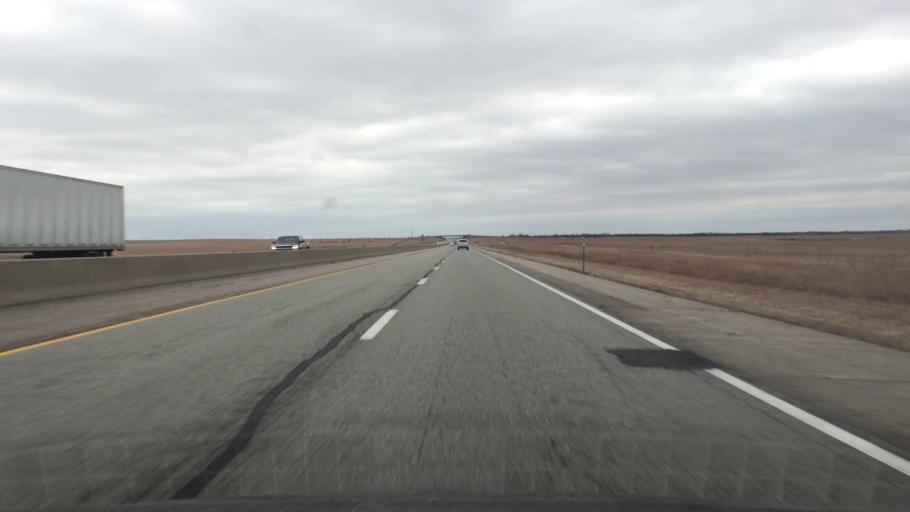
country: US
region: Kansas
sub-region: Butler County
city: El Dorado
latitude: 37.9968
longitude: -96.6944
